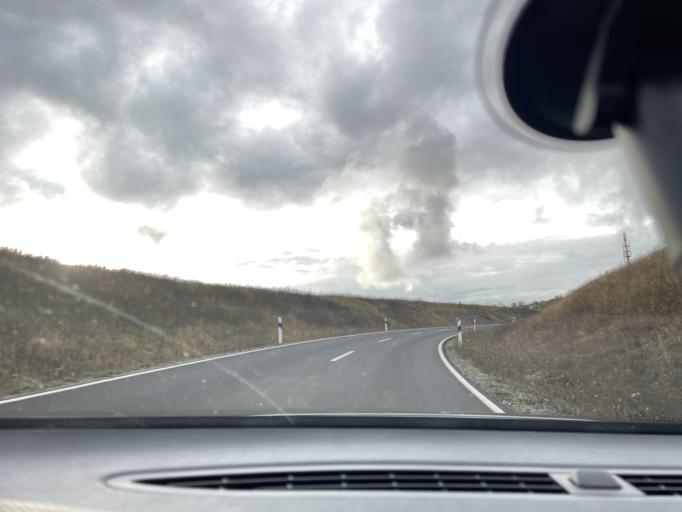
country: DE
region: Bavaria
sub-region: Regierungsbezirk Unterfranken
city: Rodelmaier
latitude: 50.2951
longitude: 10.2793
